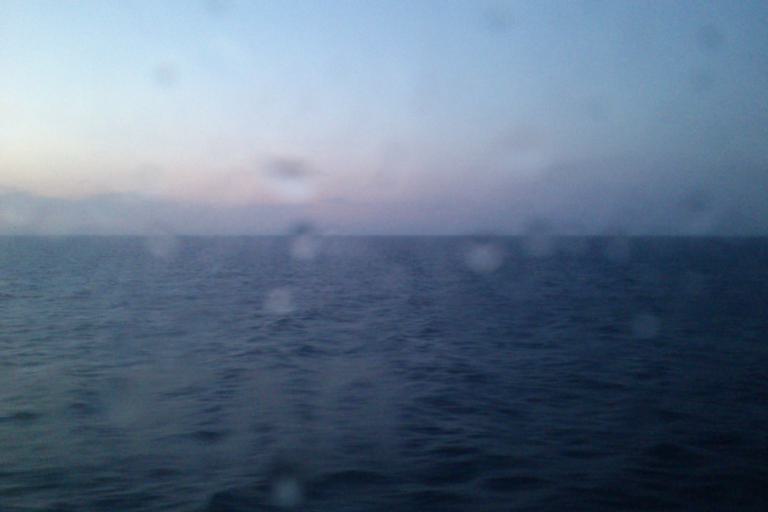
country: JP
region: Ishikawa
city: Kanazawa-shi
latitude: 37.0739
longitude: 136.0100
